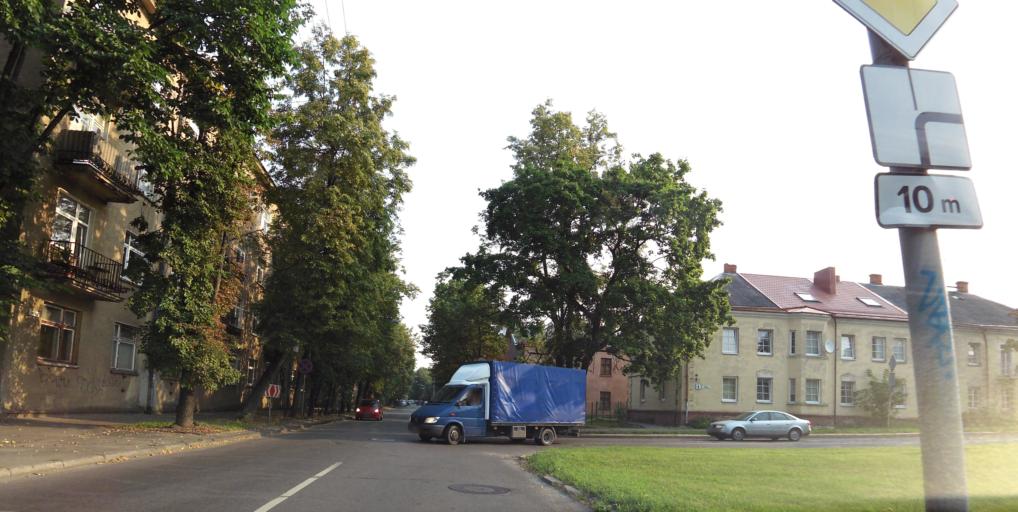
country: LT
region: Vilnius County
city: Rasos
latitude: 54.7048
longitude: 25.3129
